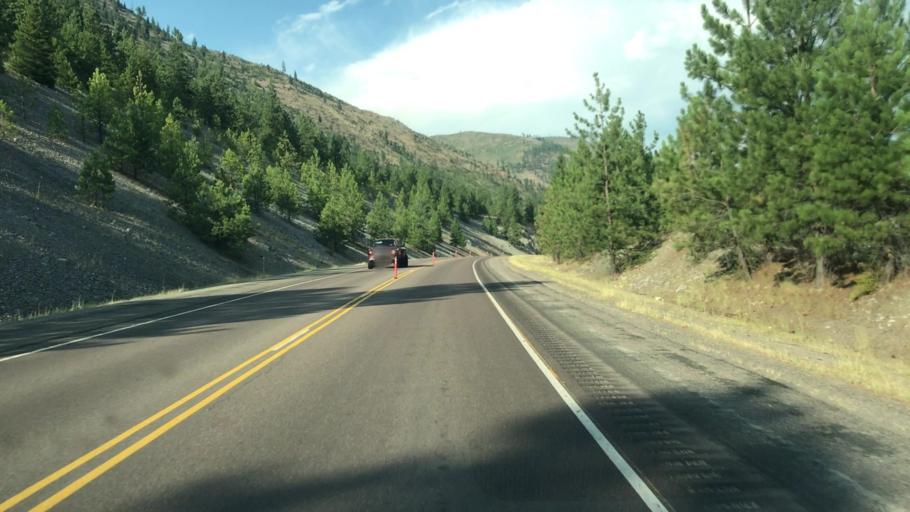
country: US
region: Montana
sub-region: Mineral County
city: Superior
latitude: 47.0152
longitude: -114.6923
